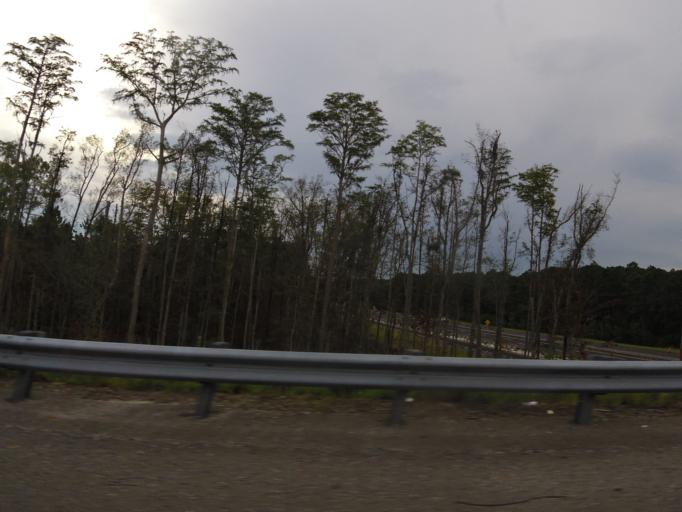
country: US
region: Florida
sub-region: Duval County
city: Baldwin
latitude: 30.3056
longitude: -81.8831
